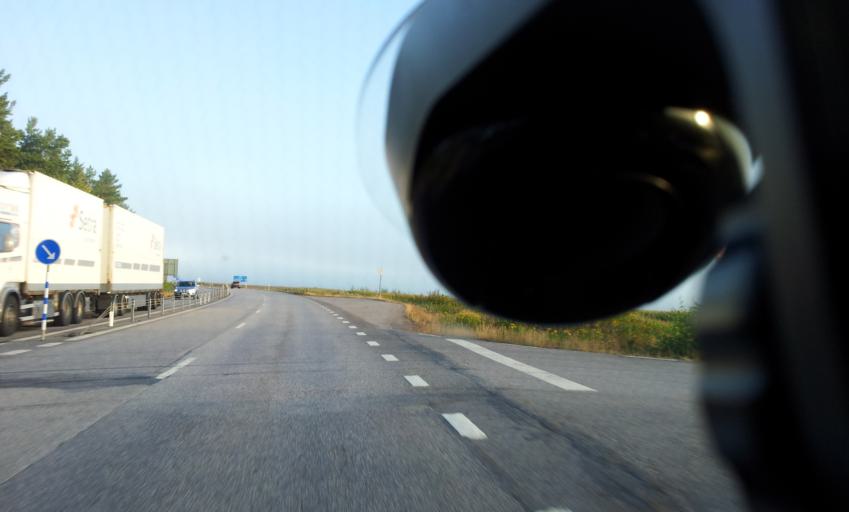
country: SE
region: Kalmar
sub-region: Vasterviks Kommun
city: Vaestervik
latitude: 57.7702
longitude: 16.5555
